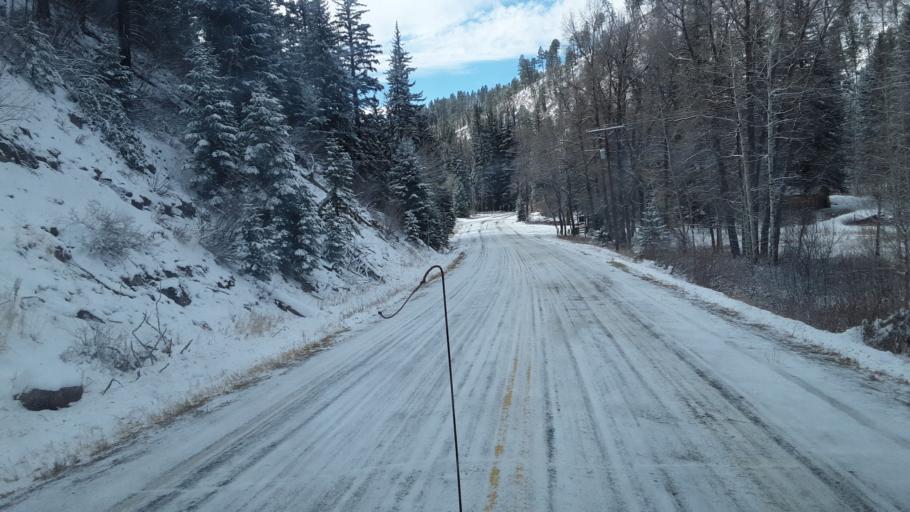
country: US
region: Colorado
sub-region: La Plata County
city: Bayfield
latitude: 37.3724
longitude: -107.6628
